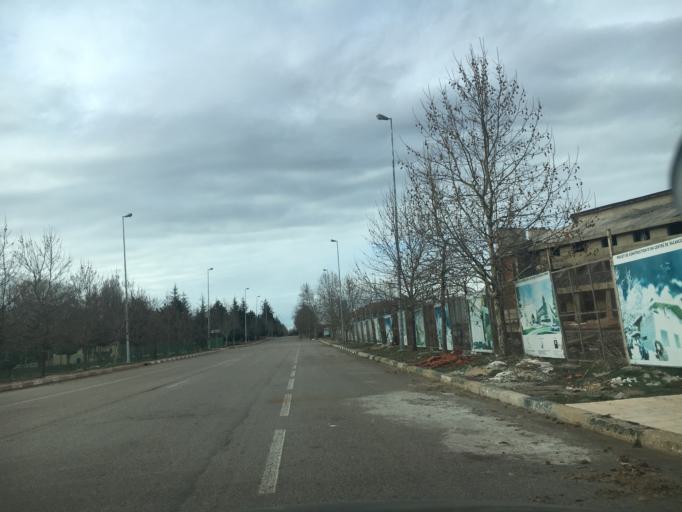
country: MA
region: Meknes-Tafilalet
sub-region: Ifrane
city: Ifrane
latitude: 33.5238
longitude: -5.1328
